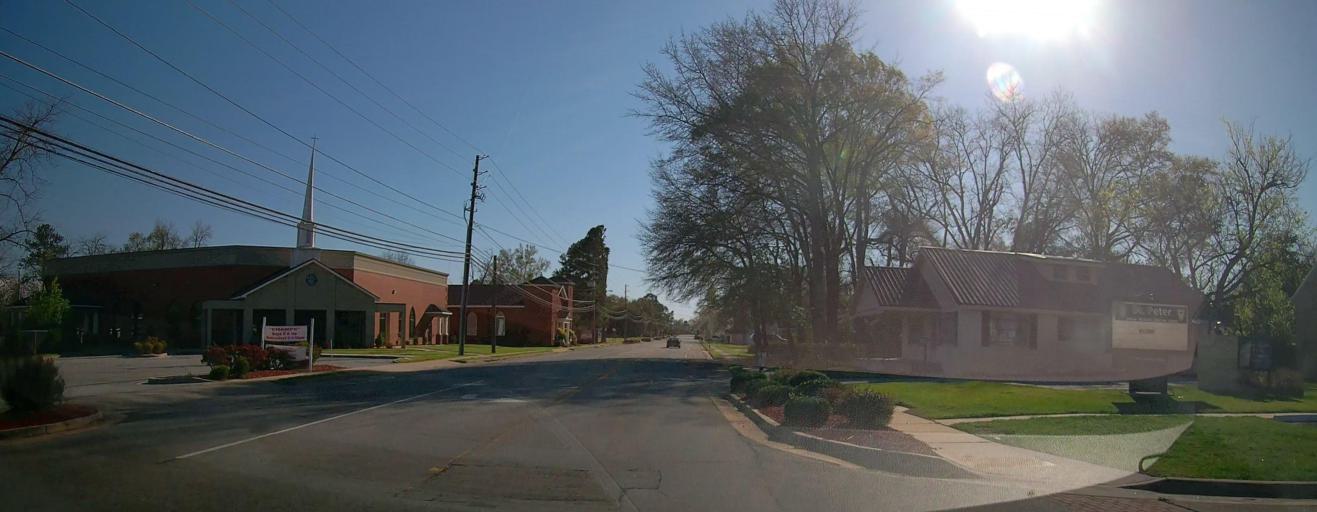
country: US
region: Georgia
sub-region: Peach County
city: Fort Valley
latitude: 32.5460
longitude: -83.8917
